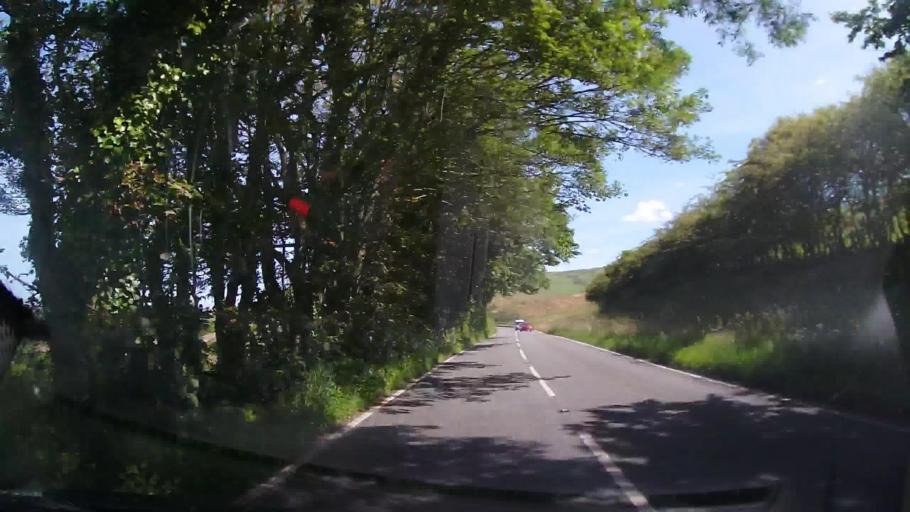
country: GB
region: Wales
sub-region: Gwynedd
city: Tywyn
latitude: 52.5674
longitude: -4.0721
